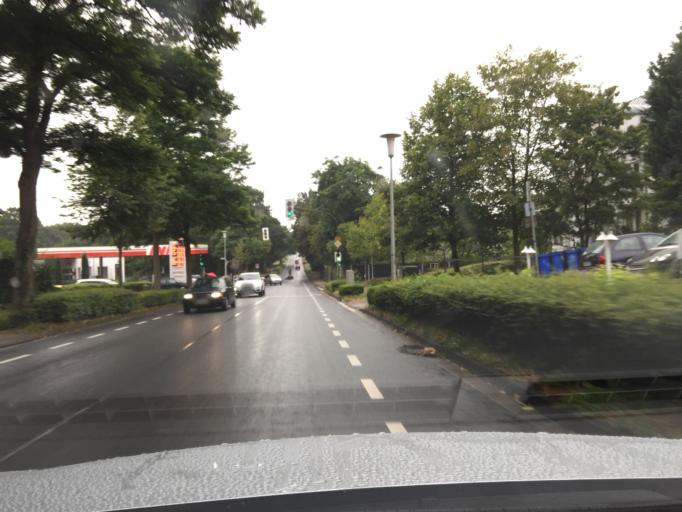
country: DE
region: North Rhine-Westphalia
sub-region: Regierungsbezirk Dusseldorf
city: Ratingen
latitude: 51.3331
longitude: 6.9050
